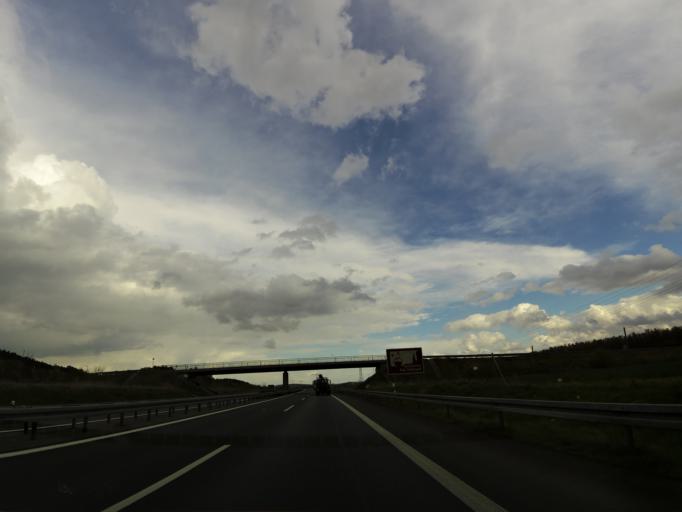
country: DE
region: Saxony-Anhalt
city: Blankenburg
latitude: 51.8067
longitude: 10.9577
